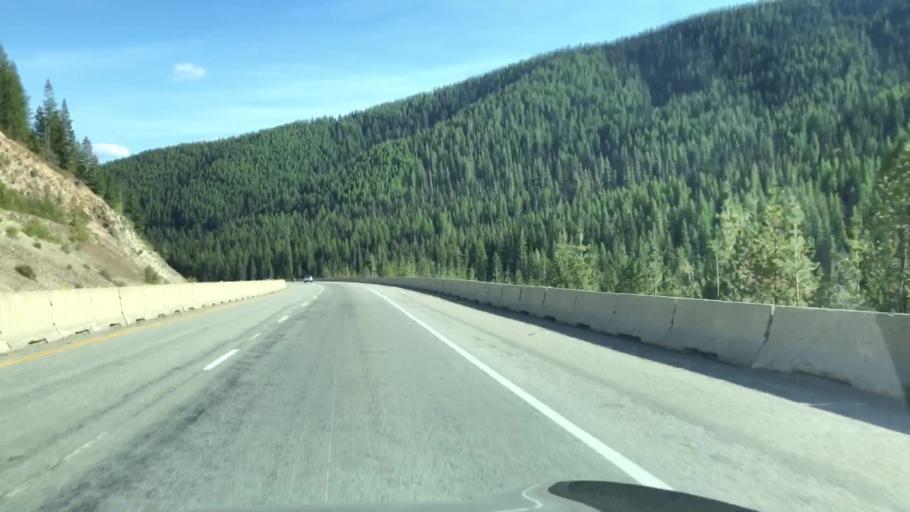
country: US
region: Idaho
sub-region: Shoshone County
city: Wallace
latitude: 47.4388
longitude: -115.6833
